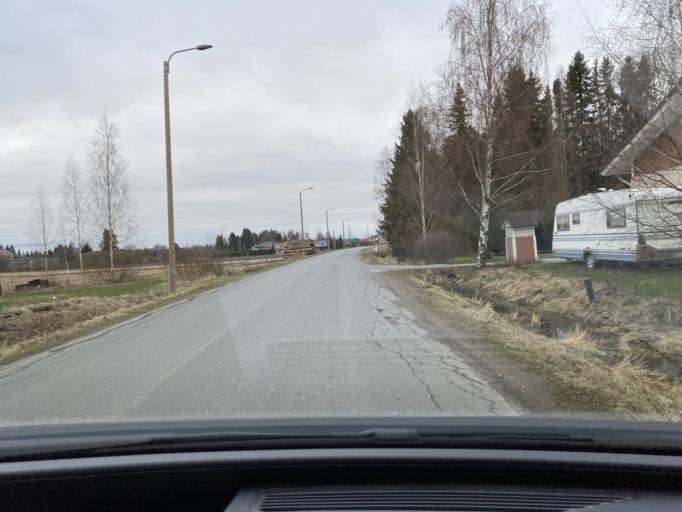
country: FI
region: Satakunta
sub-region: Pori
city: Huittinen
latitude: 61.1692
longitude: 22.7187
